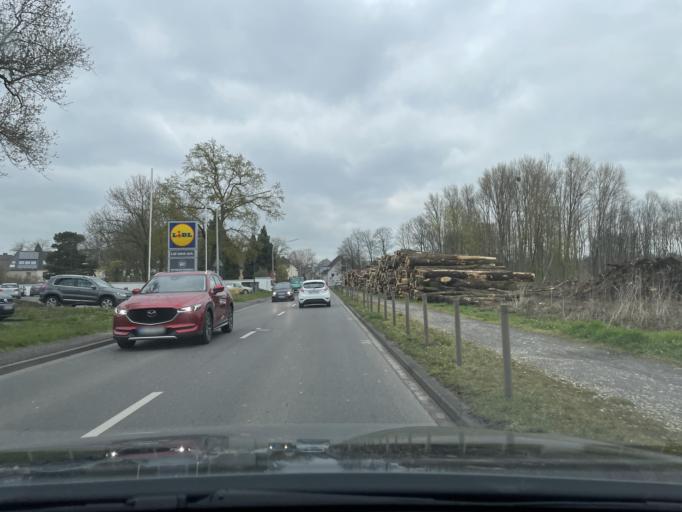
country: DE
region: North Rhine-Westphalia
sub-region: Regierungsbezirk Dusseldorf
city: Monchengladbach
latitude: 51.1646
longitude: 6.4608
